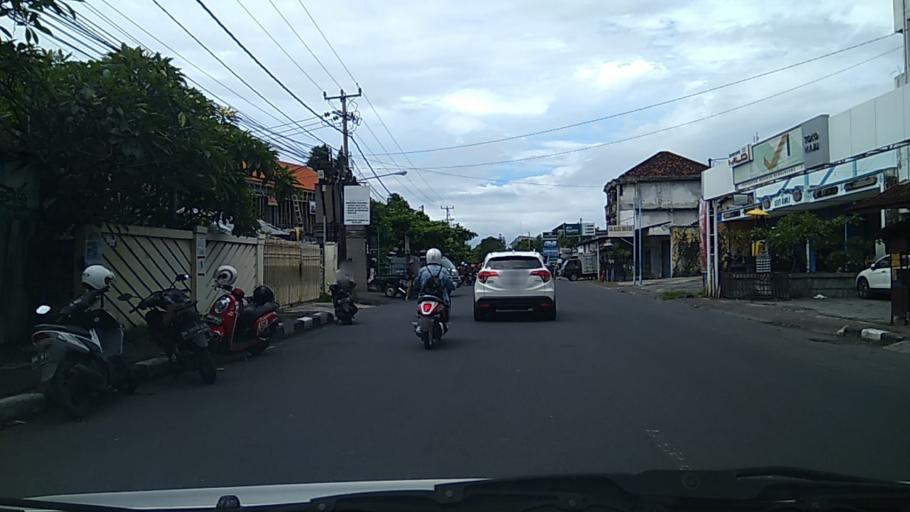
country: ID
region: Bali
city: Banjar Kertajiwa
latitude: -8.6421
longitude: 115.2509
